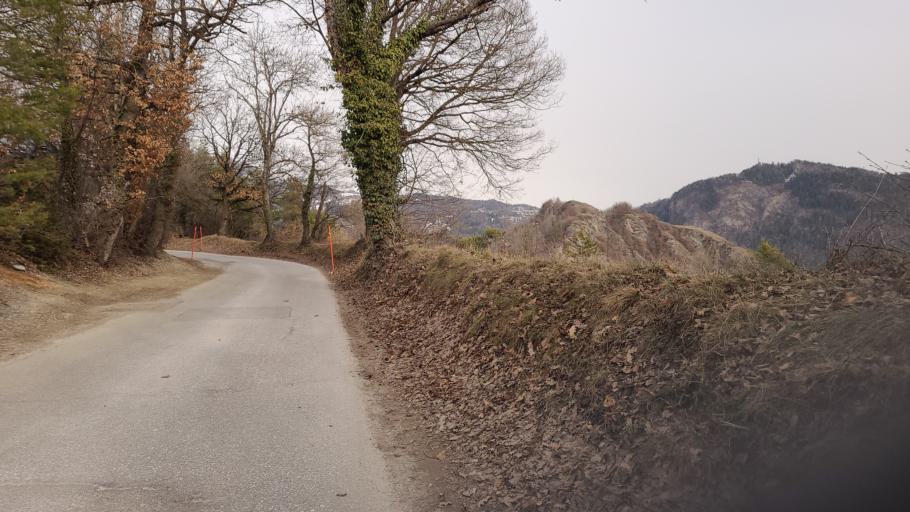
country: CH
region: Valais
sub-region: Herens District
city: Ayent
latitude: 46.2695
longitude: 7.4031
